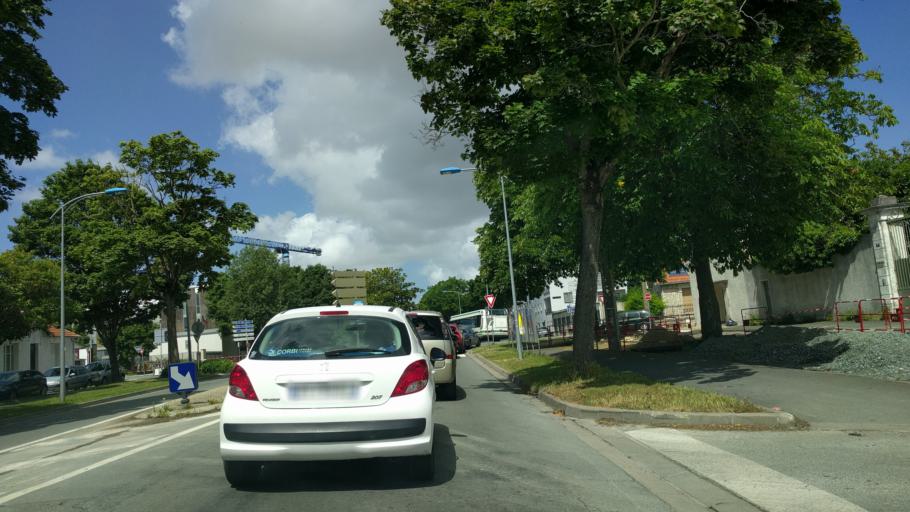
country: FR
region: Poitou-Charentes
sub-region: Departement de la Charente-Maritime
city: La Rochelle
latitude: 46.1673
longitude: -1.1393
